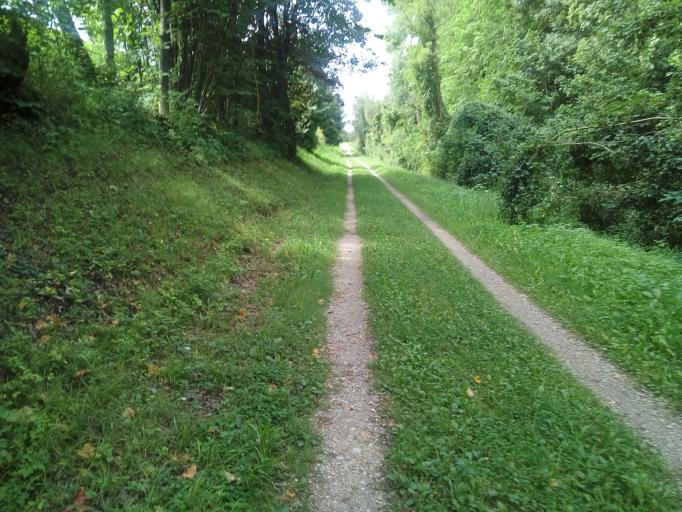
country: DE
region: Bavaria
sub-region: Upper Bavaria
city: Unterfoehring
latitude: 48.1984
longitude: 11.6410
